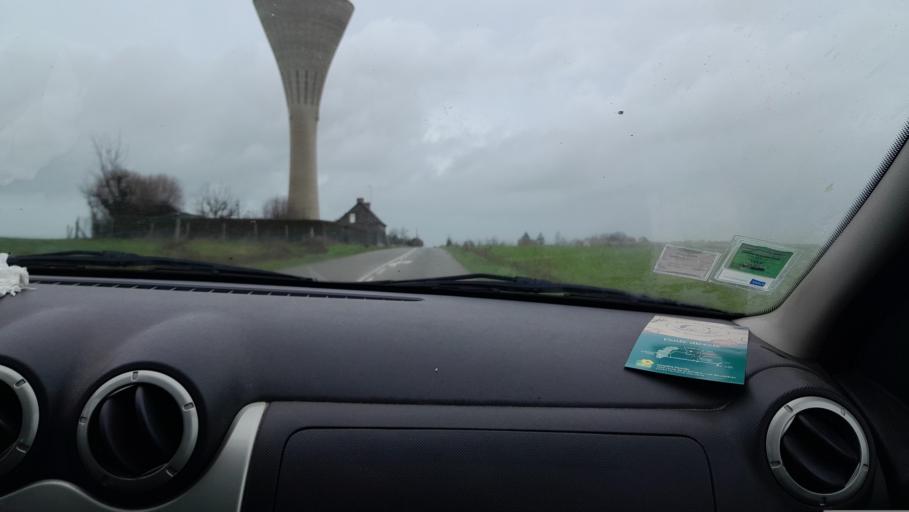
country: FR
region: Pays de la Loire
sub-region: Departement de la Mayenne
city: Ballots
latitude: 47.9084
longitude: -1.1024
